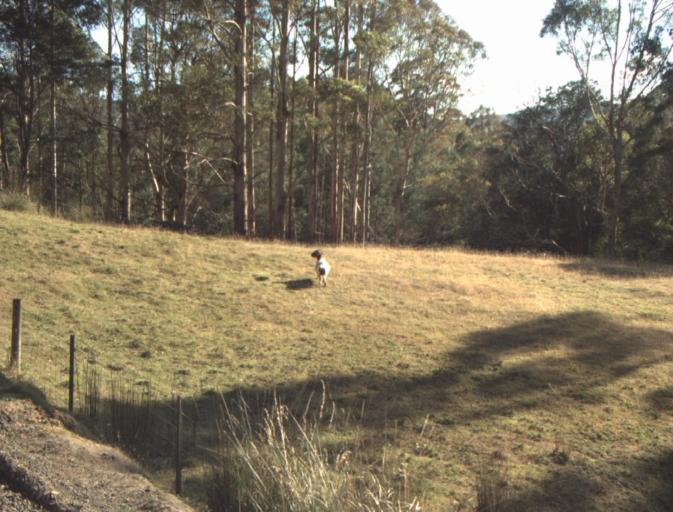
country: AU
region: Tasmania
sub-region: Launceston
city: Mayfield
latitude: -41.2982
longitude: 147.1980
